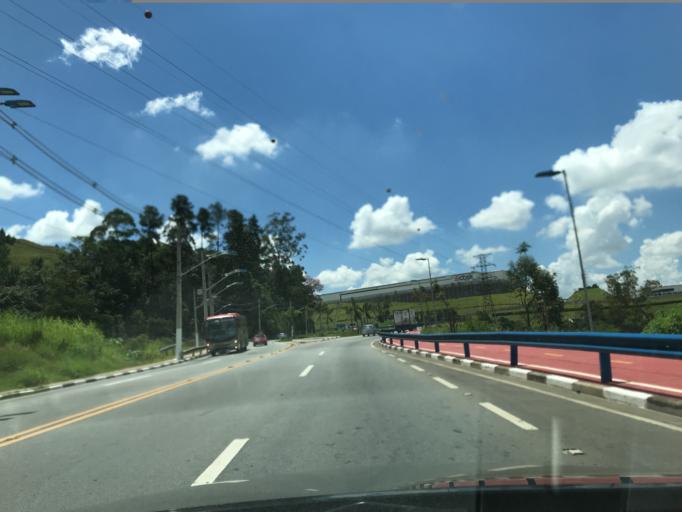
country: BR
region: Sao Paulo
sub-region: Itapevi
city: Itapevi
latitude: -23.5337
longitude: -46.9376
